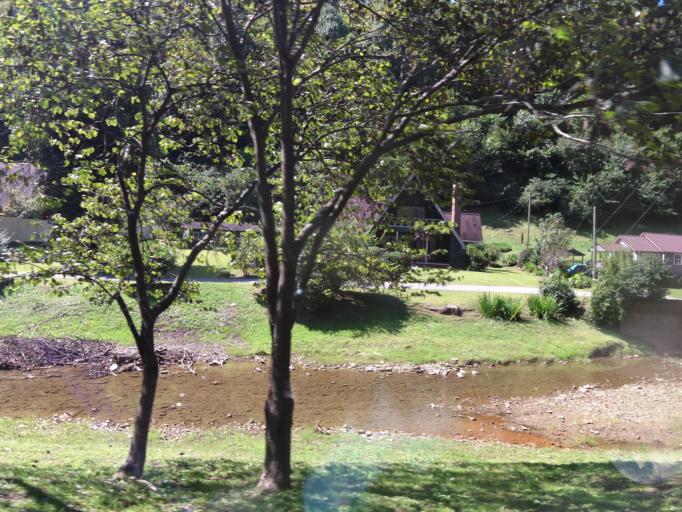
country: US
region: Kentucky
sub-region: Leslie County
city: Hyden
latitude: 37.1480
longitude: -83.4064
